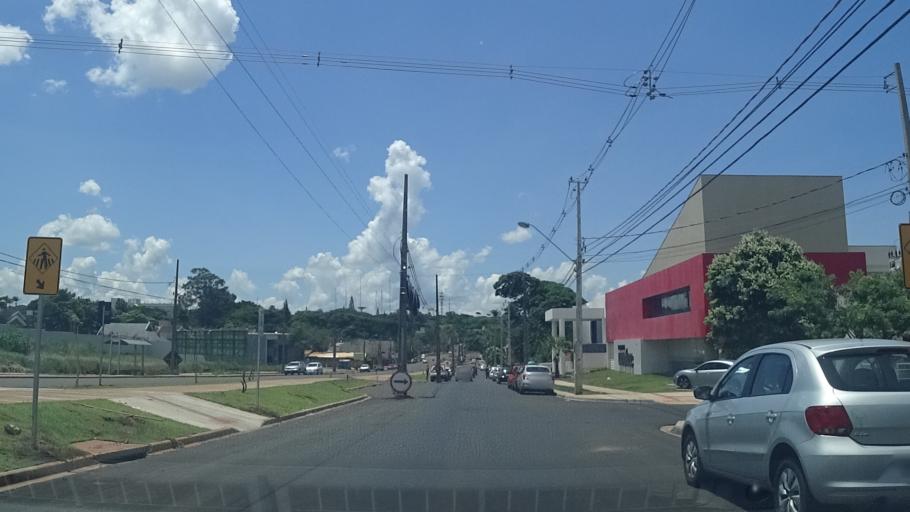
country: BR
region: Parana
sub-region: Maringa
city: Maringa
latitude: -23.4406
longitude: -51.9559
